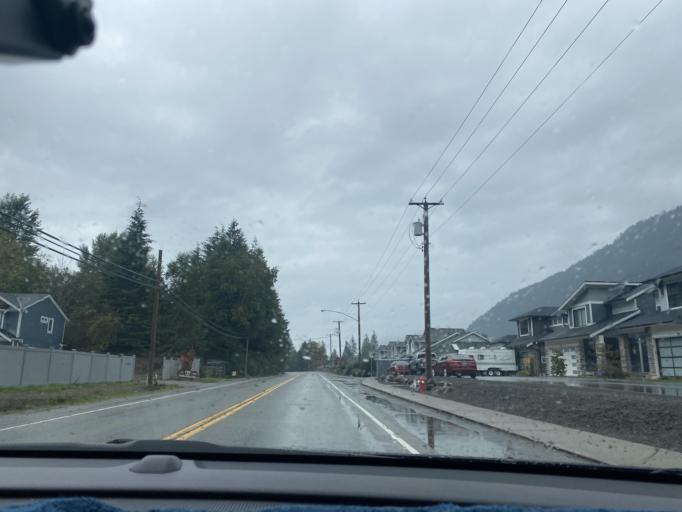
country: CA
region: British Columbia
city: Agassiz
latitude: 49.2890
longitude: -121.7801
